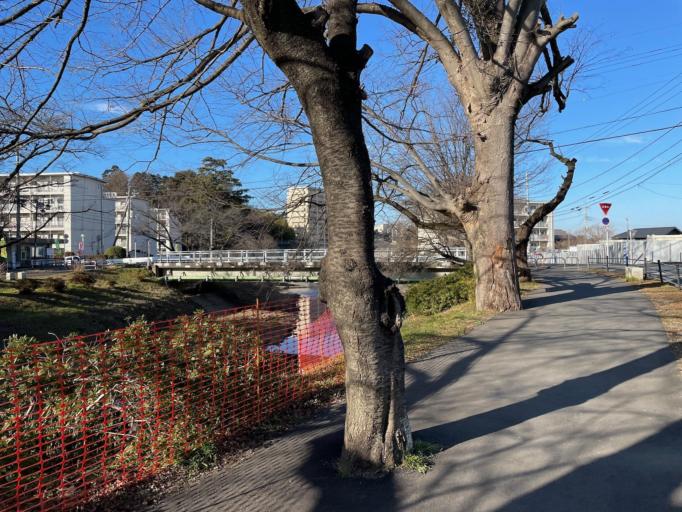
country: JP
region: Saitama
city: Sayama
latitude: 35.8344
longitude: 139.3827
